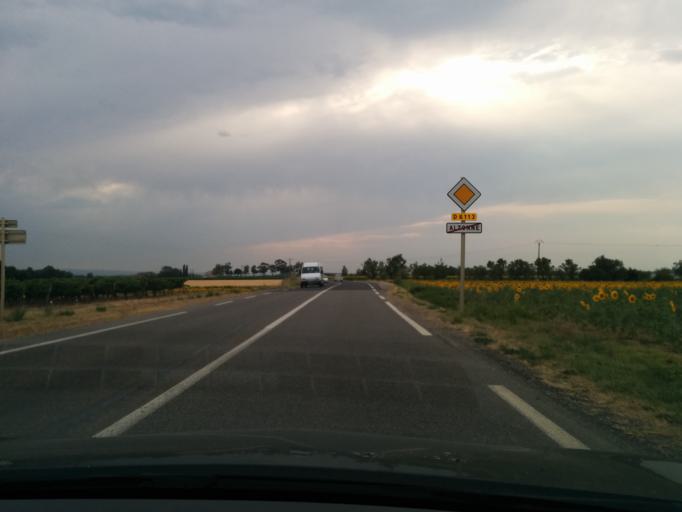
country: FR
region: Languedoc-Roussillon
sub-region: Departement de l'Aude
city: Alzonne
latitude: 43.2548
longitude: 2.1661
